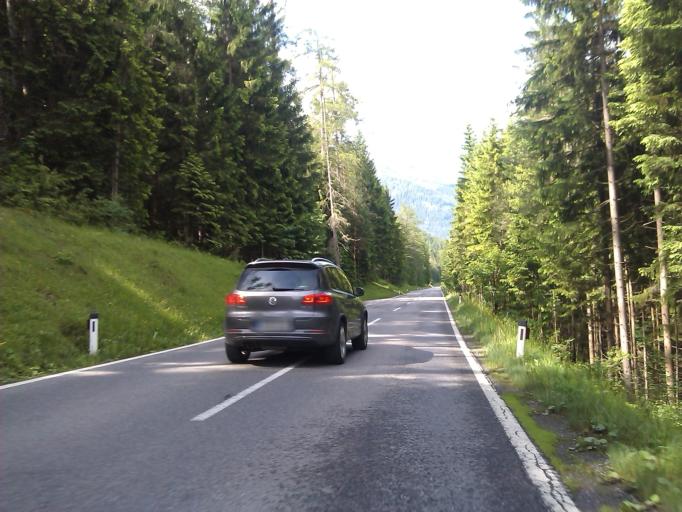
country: AT
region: Tyrol
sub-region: Politischer Bezirk Reutte
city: Ehrwald
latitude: 47.3892
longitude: 10.9126
